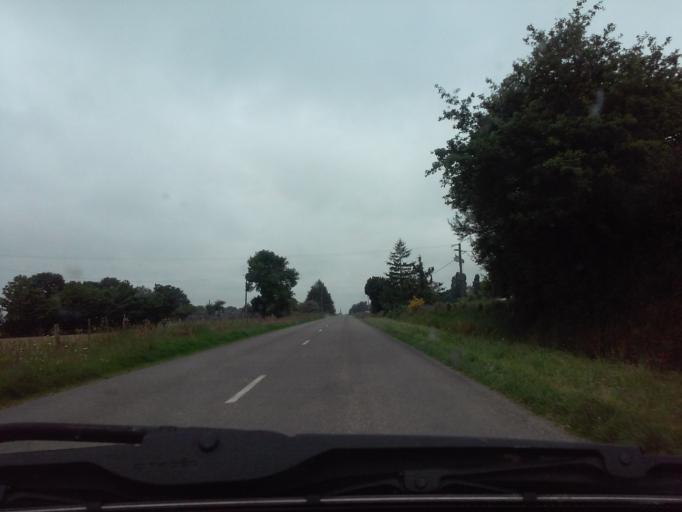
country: FR
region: Brittany
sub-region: Departement d'Ille-et-Vilaine
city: Le Pertre
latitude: 47.9633
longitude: -1.0186
